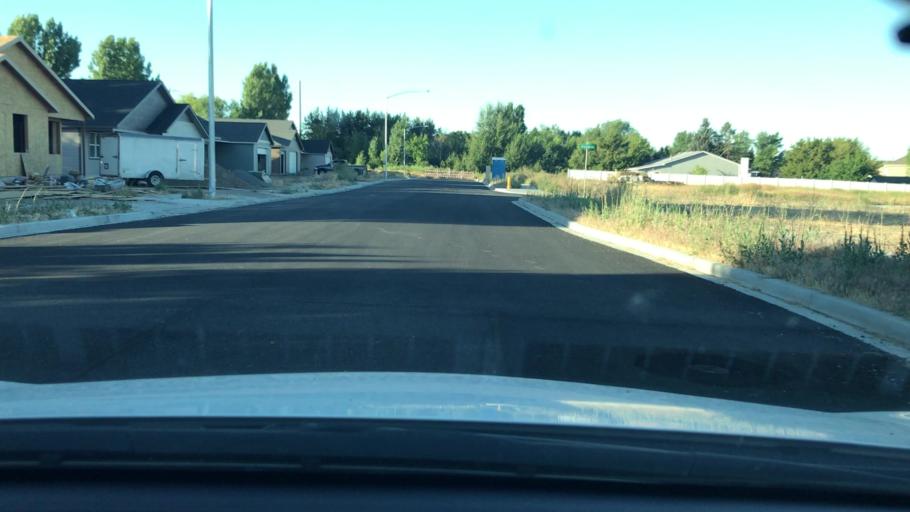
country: US
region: Washington
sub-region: Grant County
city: Moses Lake
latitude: 47.1195
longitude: -119.2524
